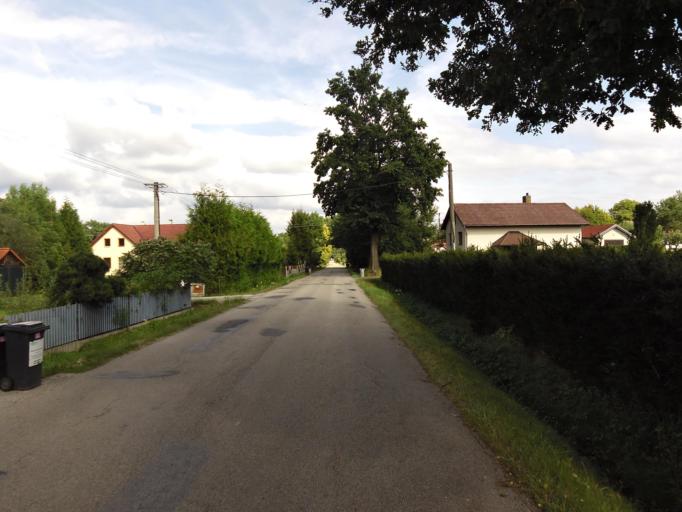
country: CZ
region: Jihocesky
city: Suchdol nad Luznici
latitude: 48.8896
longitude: 14.8548
